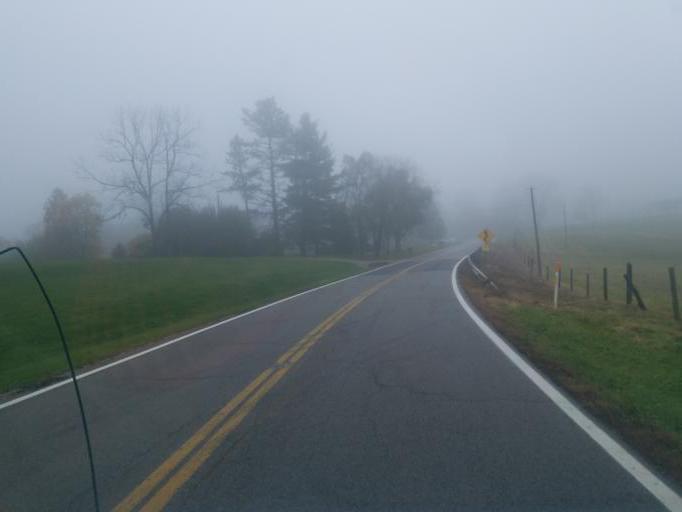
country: US
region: Ohio
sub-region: Morgan County
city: McConnelsville
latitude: 39.6203
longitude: -81.8802
